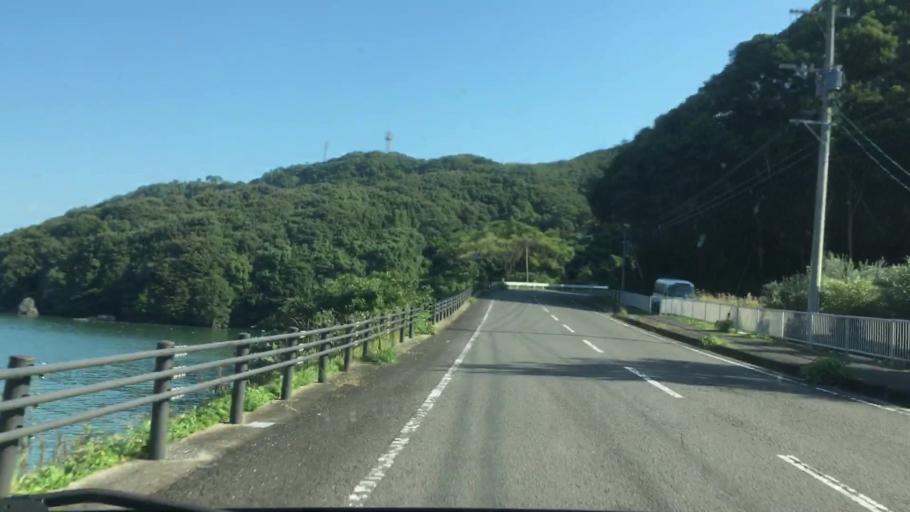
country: JP
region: Nagasaki
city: Sasebo
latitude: 32.9895
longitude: 129.6471
